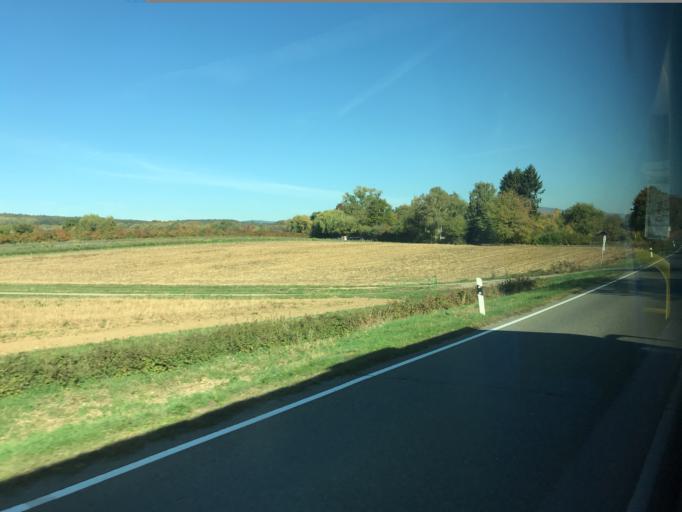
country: DE
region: Hesse
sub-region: Regierungsbezirk Darmstadt
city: Kriftel
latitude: 50.1016
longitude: 8.4680
